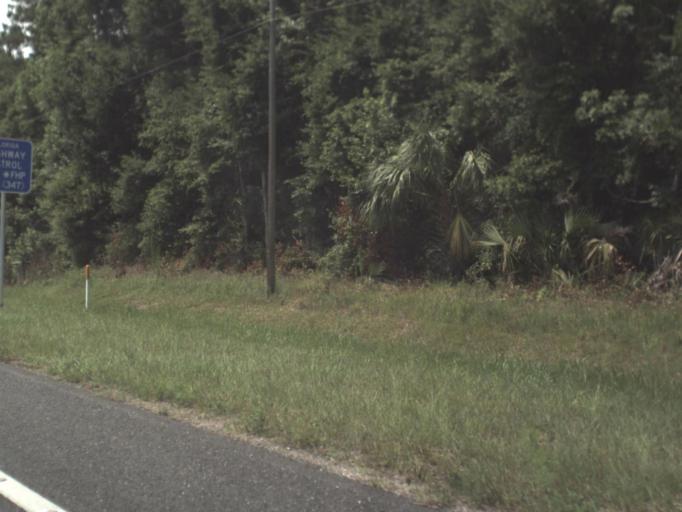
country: US
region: Florida
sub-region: Levy County
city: Chiefland
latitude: 29.4631
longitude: -82.8518
